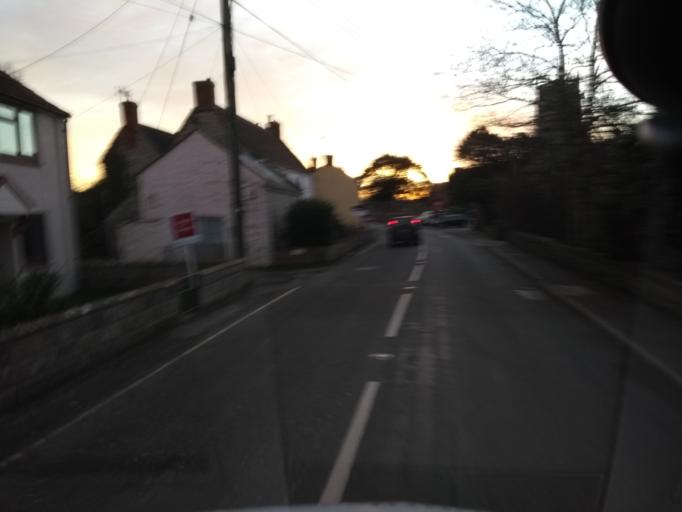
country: GB
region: England
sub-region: Somerset
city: Wedmore
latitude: 51.2270
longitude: -2.8897
